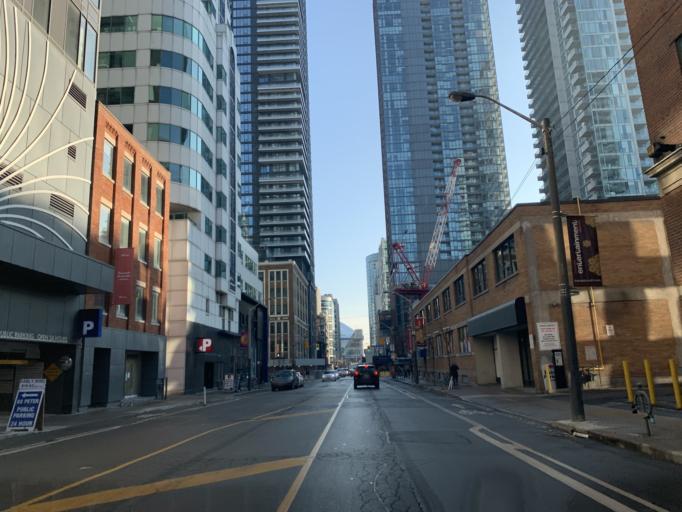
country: CA
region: Ontario
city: Toronto
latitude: 43.6469
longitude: -79.3927
